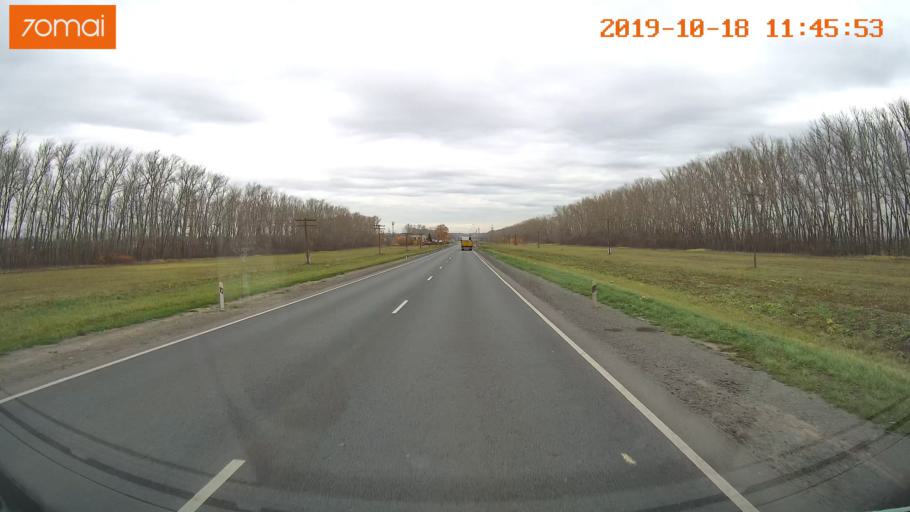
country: RU
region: Rjazan
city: Mikhaylov
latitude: 54.2146
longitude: 38.9762
